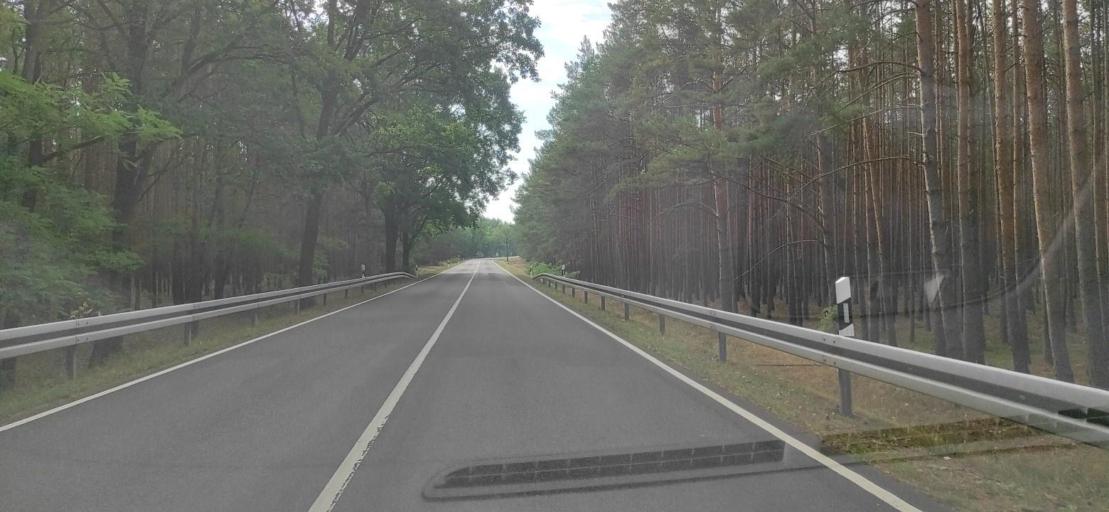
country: DE
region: Brandenburg
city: Forst
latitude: 51.6814
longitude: 14.7232
